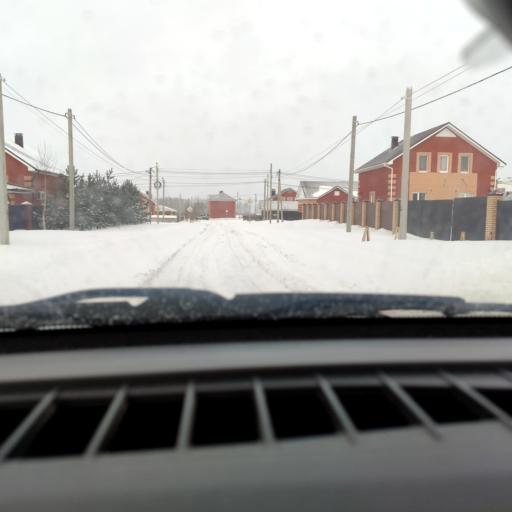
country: RU
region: Bashkortostan
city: Kabakovo
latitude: 54.6127
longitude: 56.1206
